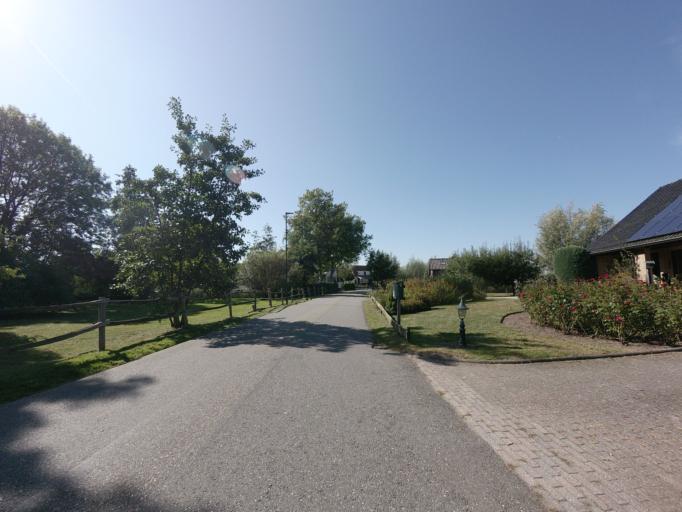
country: NL
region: South Holland
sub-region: Gemeente Giessenlanden
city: Giessenburg
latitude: 51.8708
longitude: 4.9148
